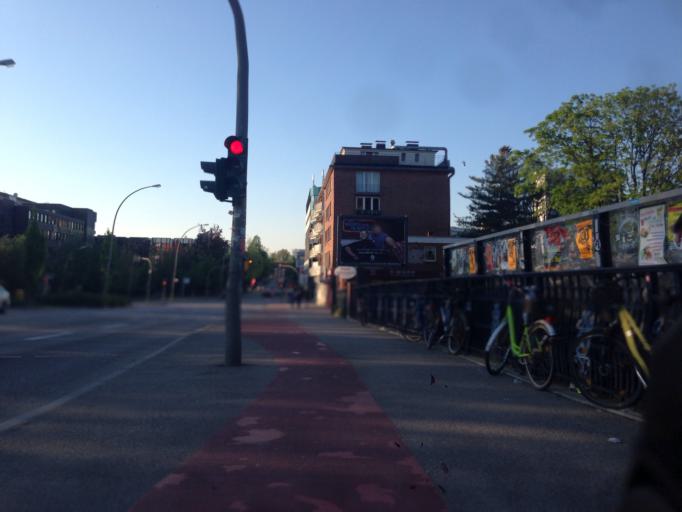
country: DE
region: Hamburg
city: Borgfelde
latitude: 53.5650
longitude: 10.0576
